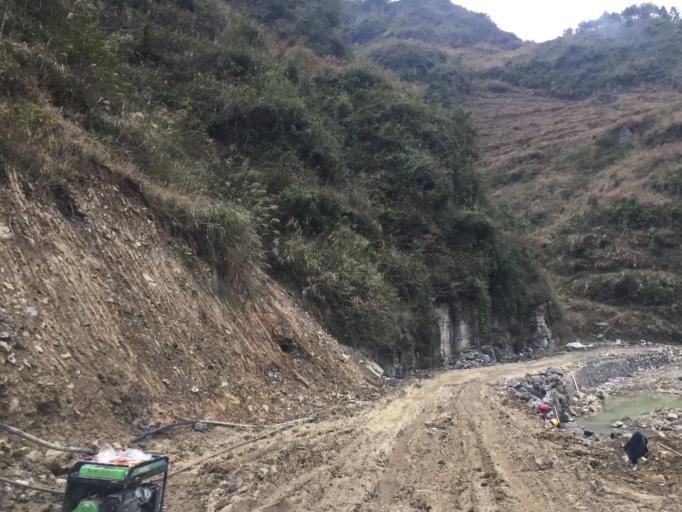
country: CN
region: Guizhou Sheng
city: Changfeng
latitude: 28.4696
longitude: 108.0809
